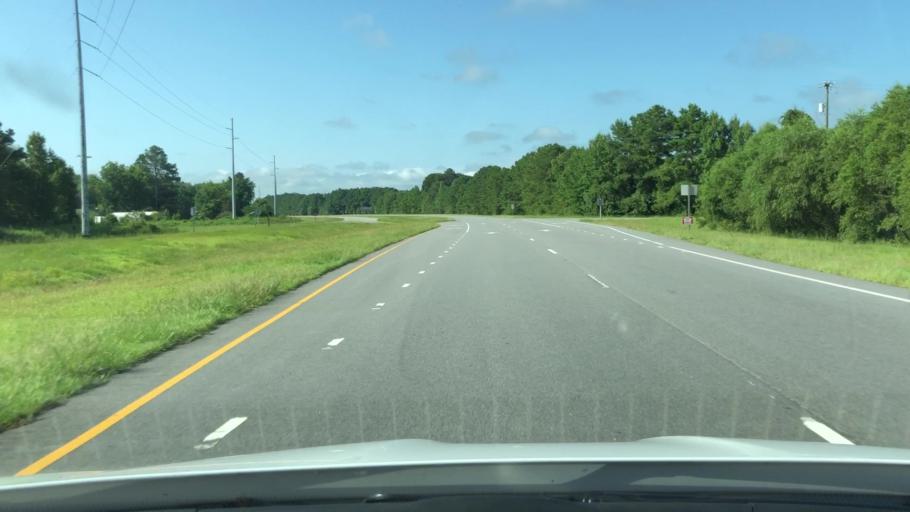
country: US
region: North Carolina
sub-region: Pasquotank County
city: Elizabeth City
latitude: 36.4474
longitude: -76.3379
